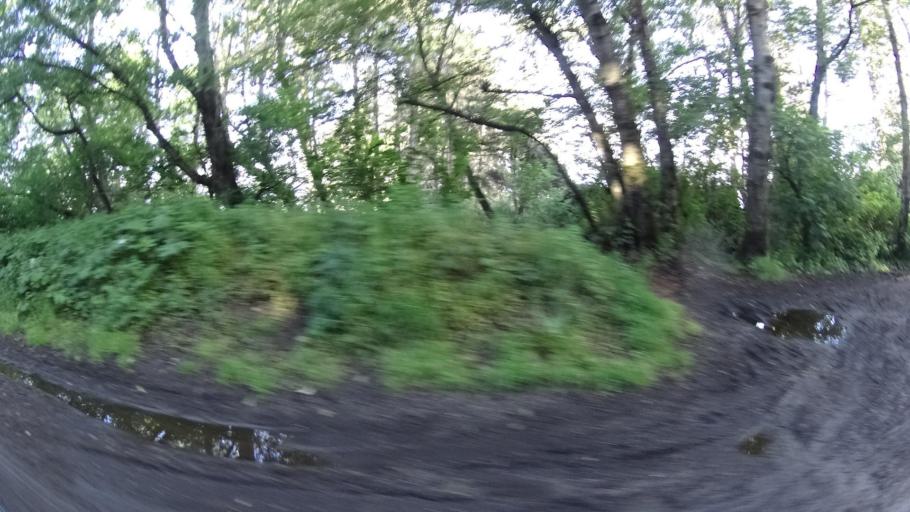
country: US
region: California
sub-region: Humboldt County
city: Westhaven-Moonstone
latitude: 41.0476
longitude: -124.1236
